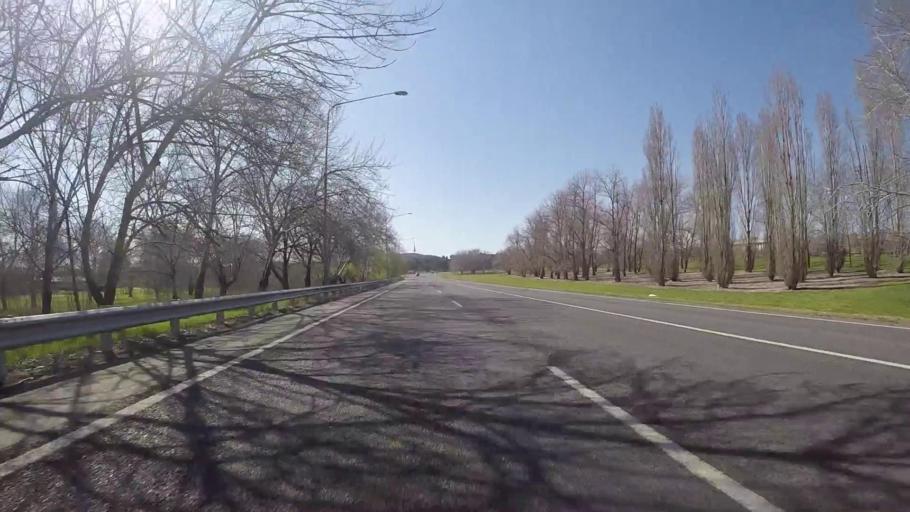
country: AU
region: Australian Capital Territory
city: Forrest
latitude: -35.3211
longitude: 149.0886
